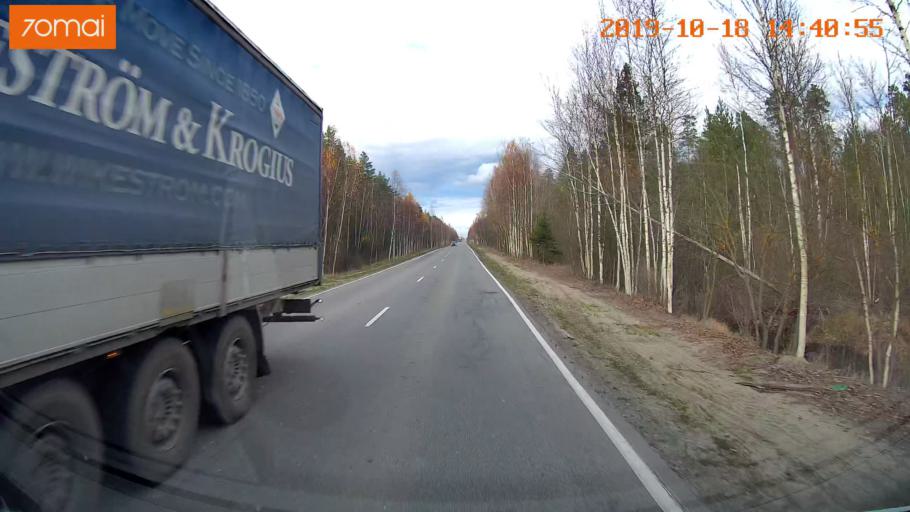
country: RU
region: Vladimir
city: Velikodvorskiy
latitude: 55.2840
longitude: 40.6699
